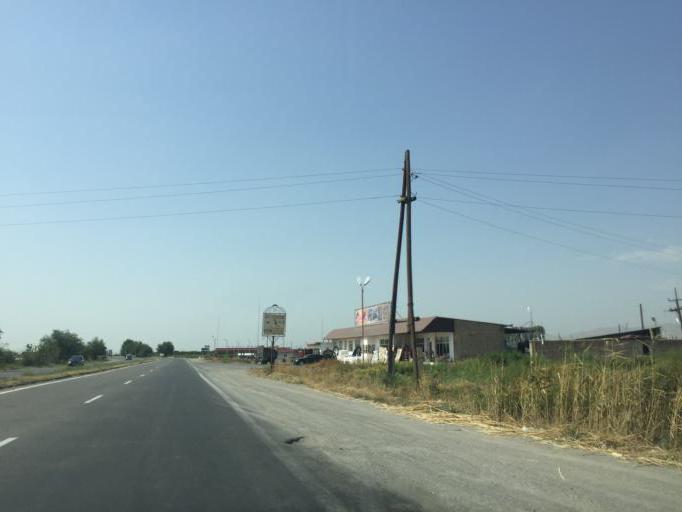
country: AM
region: Ararat
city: Aralez
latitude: 39.9044
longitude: 44.6108
